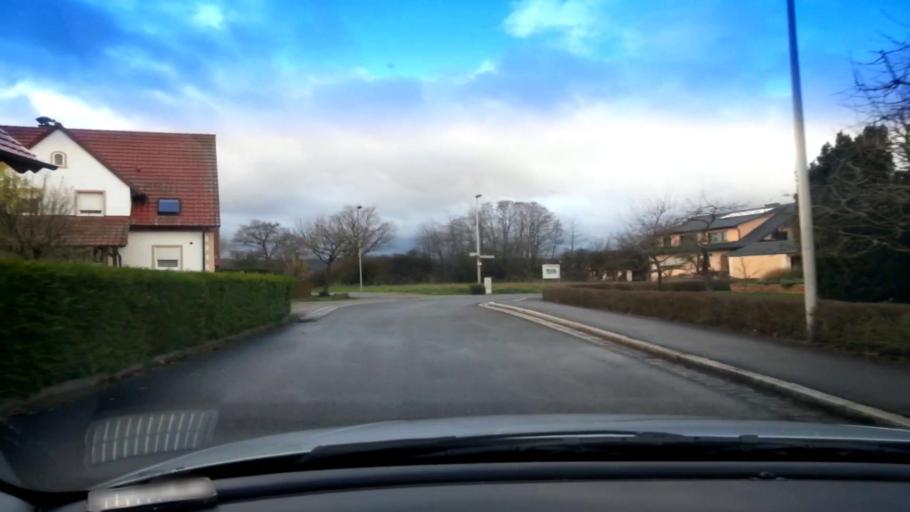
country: DE
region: Bavaria
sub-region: Upper Franconia
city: Rattelsdorf
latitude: 50.0083
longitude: 10.9009
